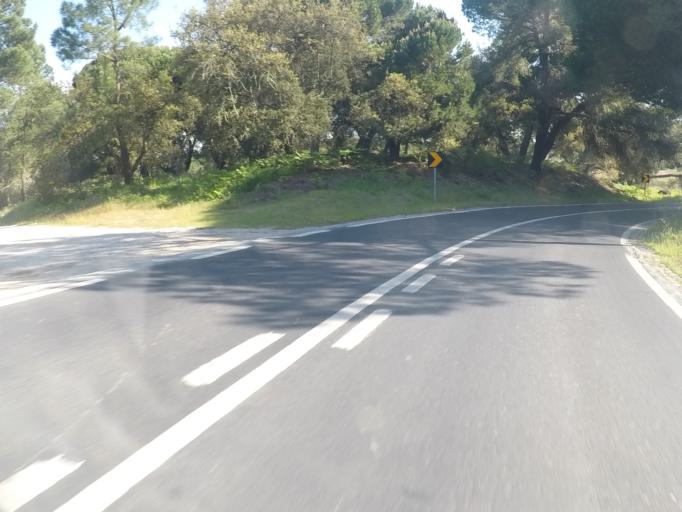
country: PT
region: Setubal
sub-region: Sesimbra
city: Sesimbra
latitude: 38.5087
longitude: -9.1479
